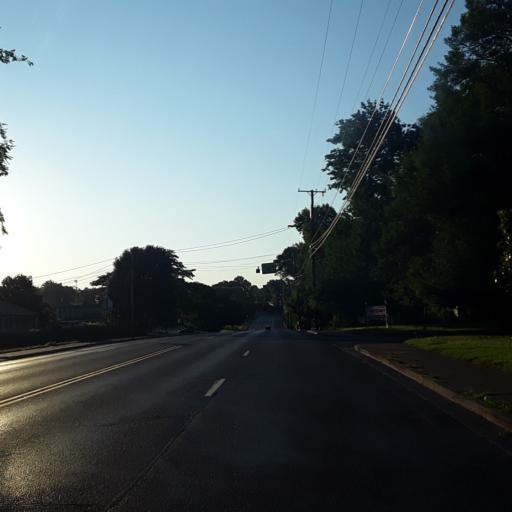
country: US
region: Tennessee
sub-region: Davidson County
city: Oak Hill
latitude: 36.1008
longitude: -86.7298
